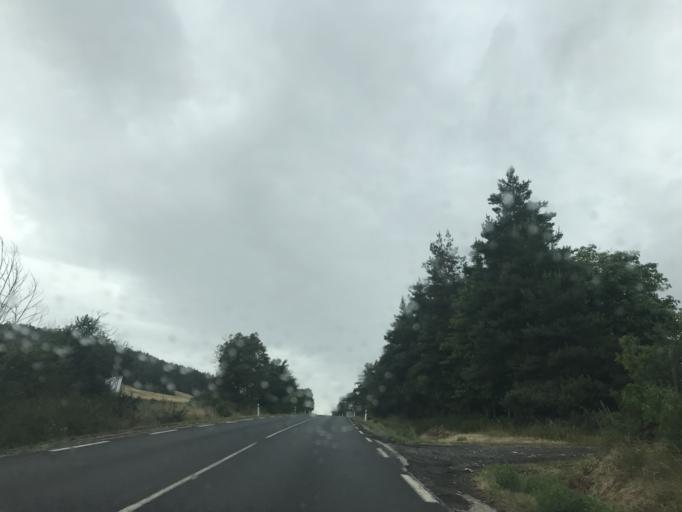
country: FR
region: Auvergne
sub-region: Departement de la Haute-Loire
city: Polignac
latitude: 45.0853
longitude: 3.8178
